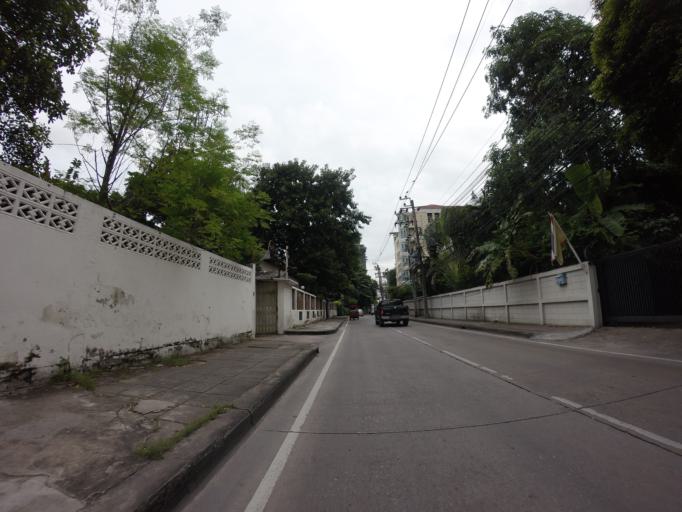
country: TH
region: Bangkok
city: Watthana
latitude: 13.7414
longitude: 100.5728
